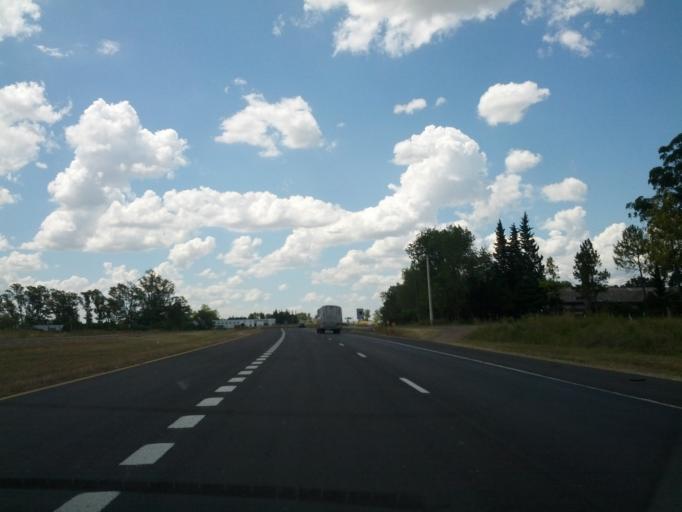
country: AR
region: Entre Rios
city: Concepcion del Uruguay
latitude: -32.5013
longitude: -58.3154
